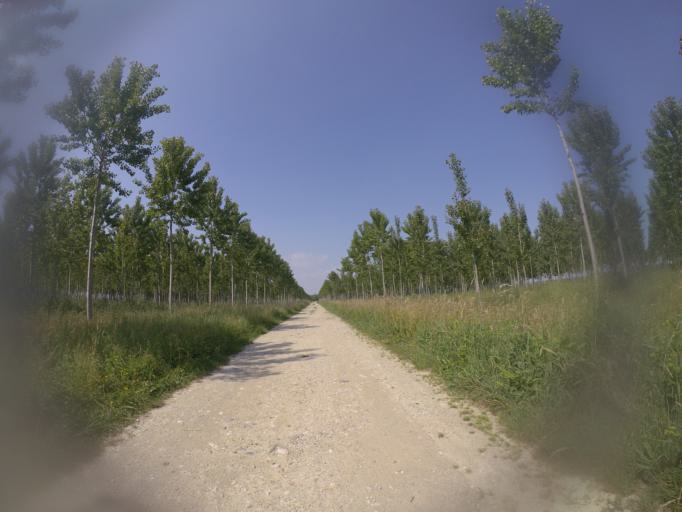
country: IT
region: Friuli Venezia Giulia
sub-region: Provincia di Udine
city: Bertiolo
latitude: 45.9305
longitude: 13.0263
